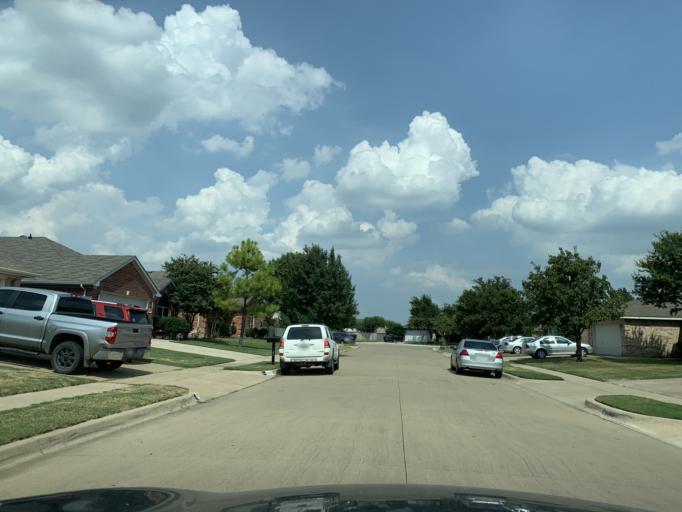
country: US
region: Texas
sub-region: Tarrant County
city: Hurst
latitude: 32.8032
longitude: -97.1964
